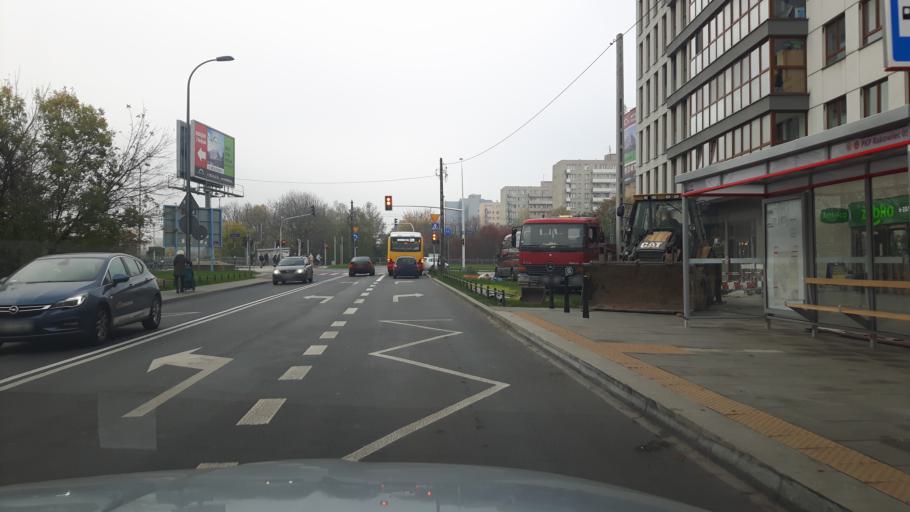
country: PL
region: Masovian Voivodeship
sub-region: Warszawa
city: Wlochy
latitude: 52.1972
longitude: 20.9629
